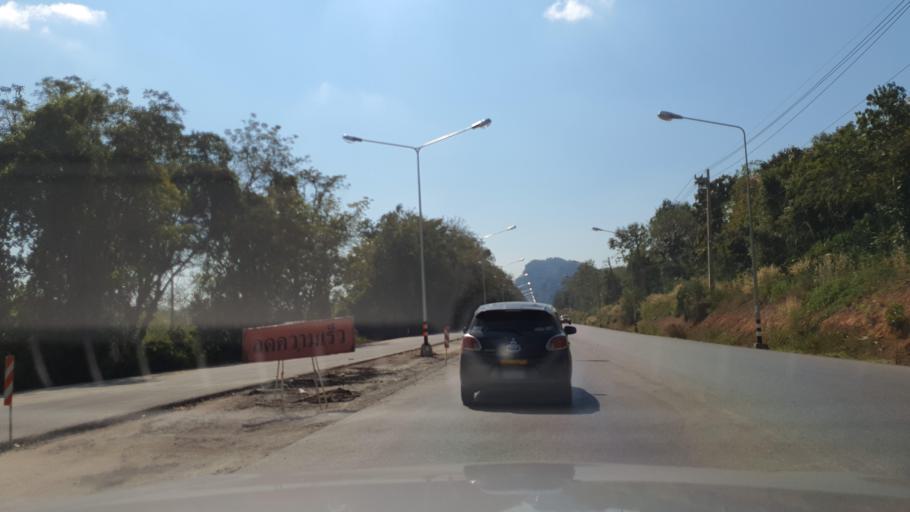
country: TH
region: Nan
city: Nan
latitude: 18.8753
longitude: 100.7446
